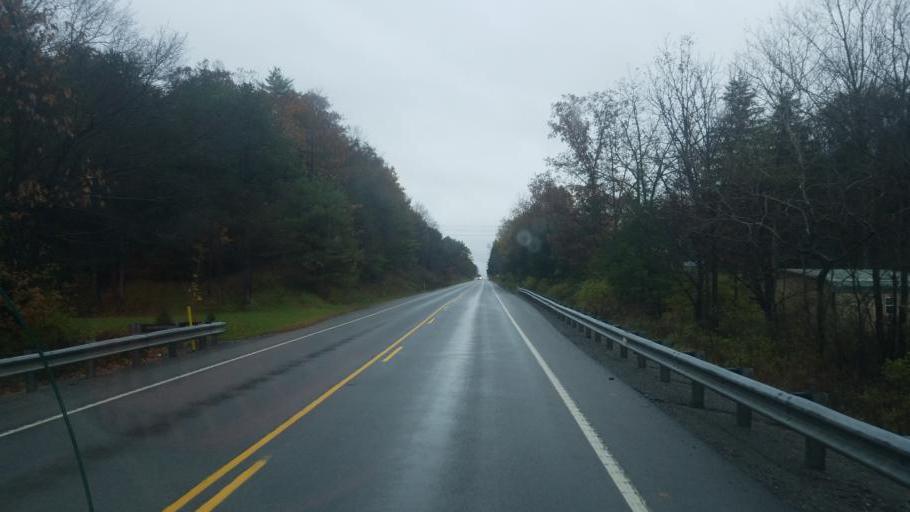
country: US
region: Pennsylvania
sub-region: Clearfield County
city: Shiloh
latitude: 41.1012
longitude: -78.2041
